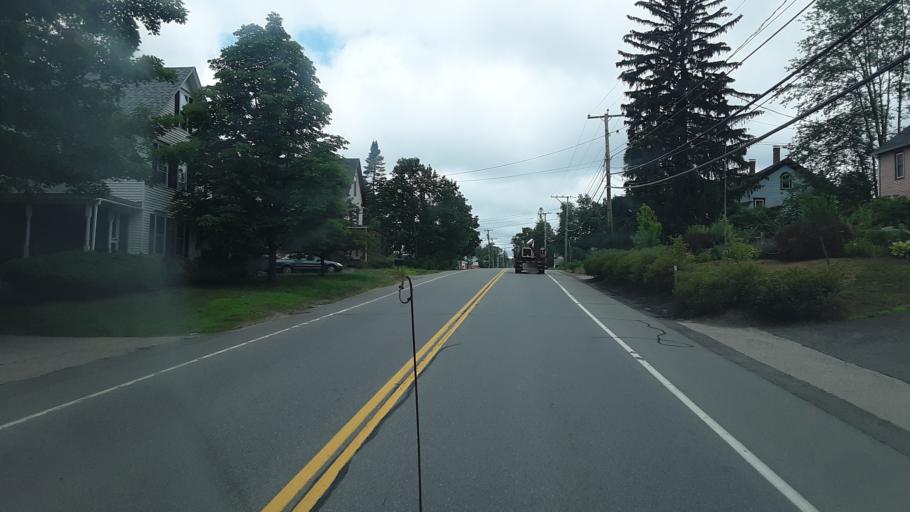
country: US
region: New Hampshire
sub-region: Rockingham County
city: Northwood
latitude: 43.1972
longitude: -71.1559
